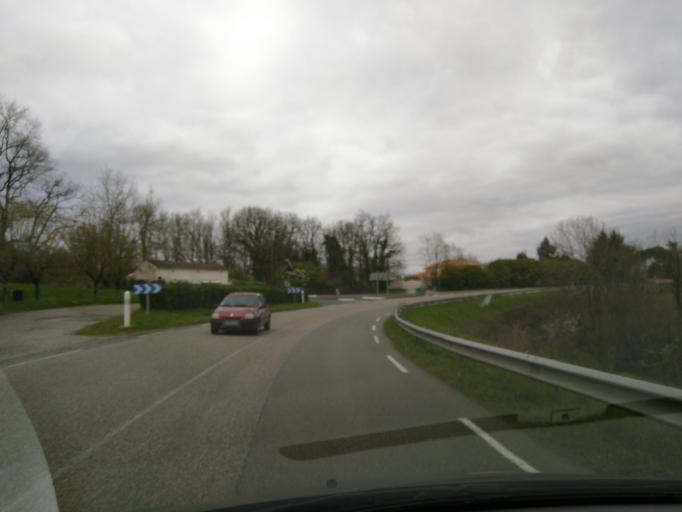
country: FR
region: Aquitaine
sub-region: Departement du Lot-et-Garonne
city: Cancon
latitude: 44.5208
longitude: 0.6206
